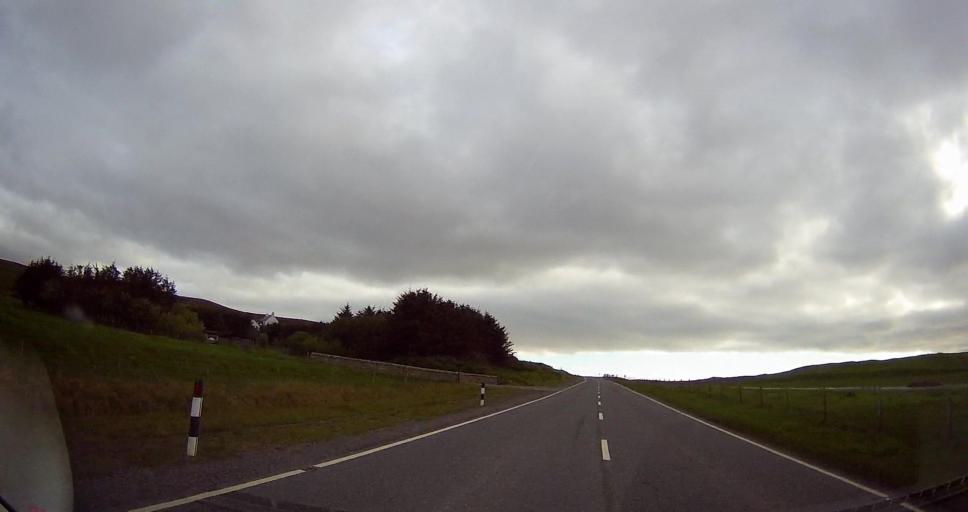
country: GB
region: Scotland
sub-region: Shetland Islands
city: Lerwick
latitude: 60.4320
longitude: -1.2951
